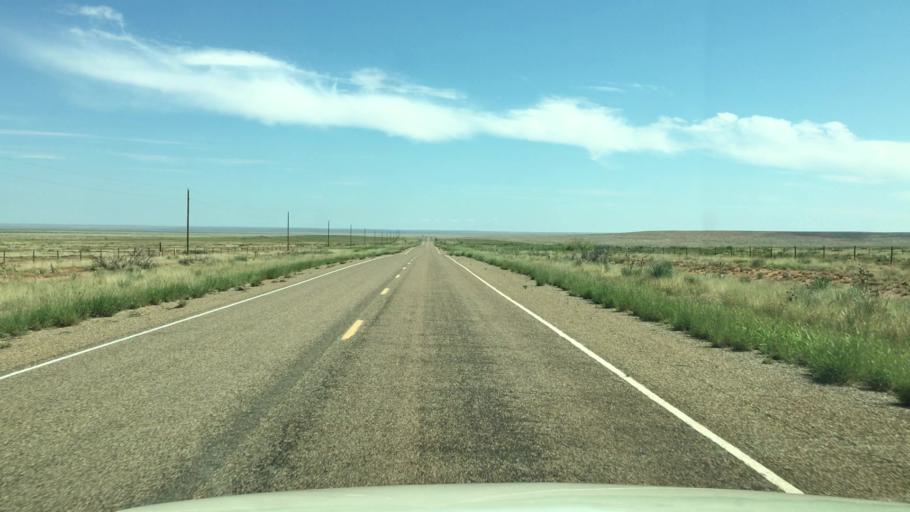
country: US
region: New Mexico
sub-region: De Baca County
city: Fort Sumner
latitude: 33.9924
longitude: -104.5697
